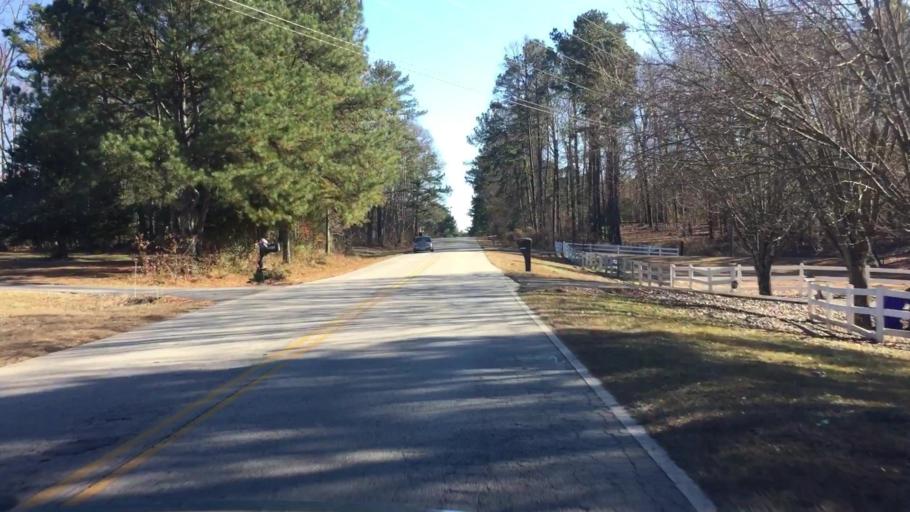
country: US
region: Georgia
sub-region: Henry County
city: McDonough
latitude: 33.4998
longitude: -84.0738
